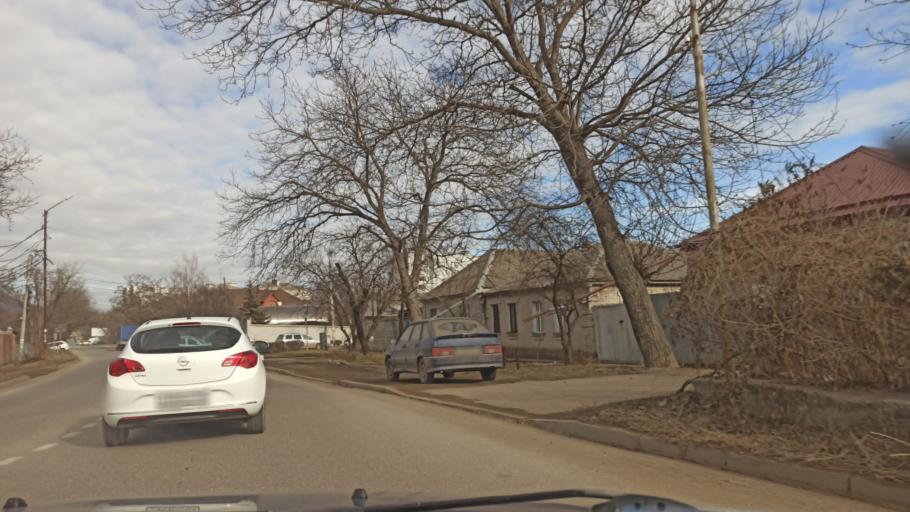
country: RU
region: Stavropol'skiy
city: Svobody
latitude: 44.0327
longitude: 43.0363
